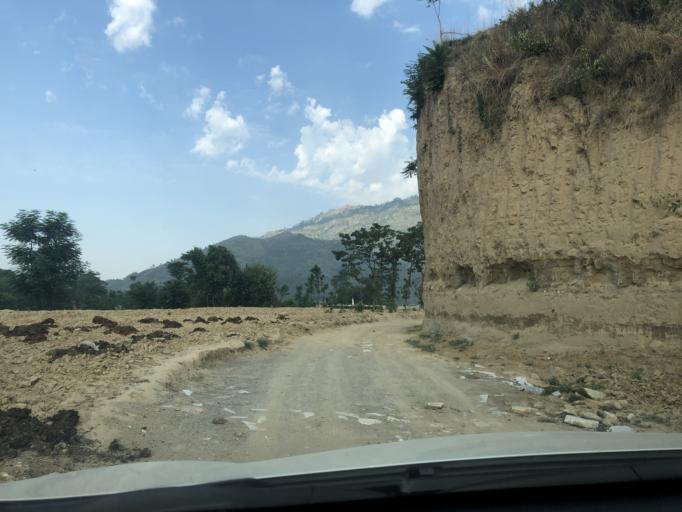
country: PK
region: Khyber Pakhtunkhwa
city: Daggar
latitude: 34.5934
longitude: 72.4548
